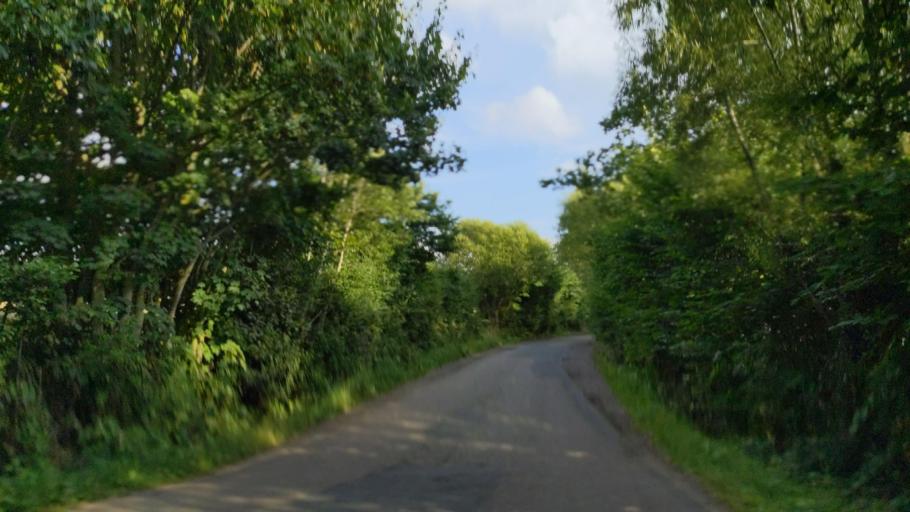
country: DE
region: Schleswig-Holstein
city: Eutin
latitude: 54.1181
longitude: 10.5906
